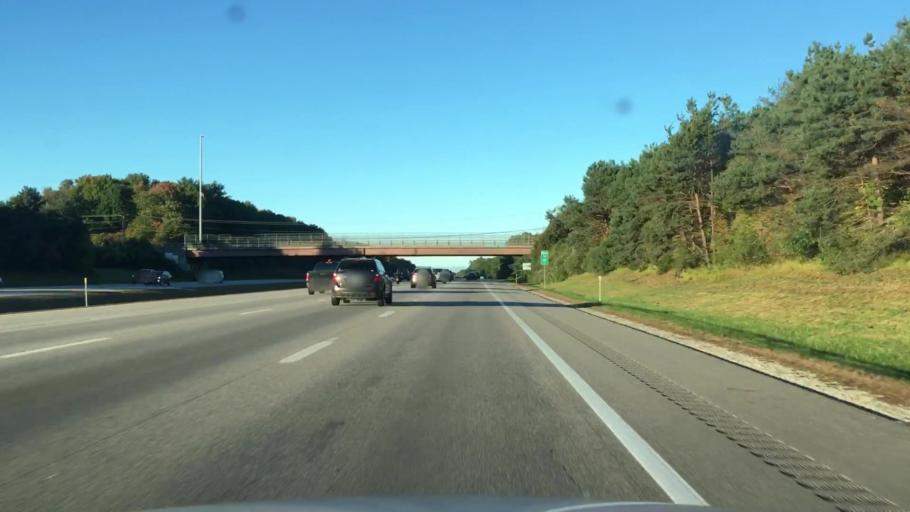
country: US
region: New Hampshire
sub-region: Rockingham County
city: Greenland
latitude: 43.0190
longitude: -70.8310
